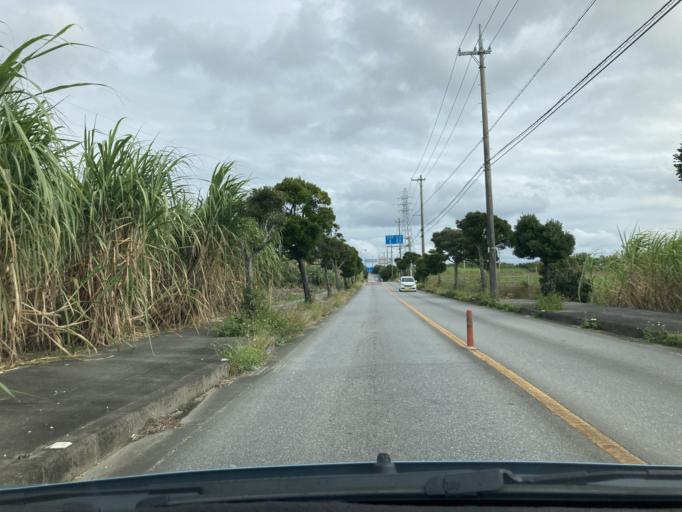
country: JP
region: Okinawa
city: Itoman
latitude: 26.1194
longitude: 127.6862
